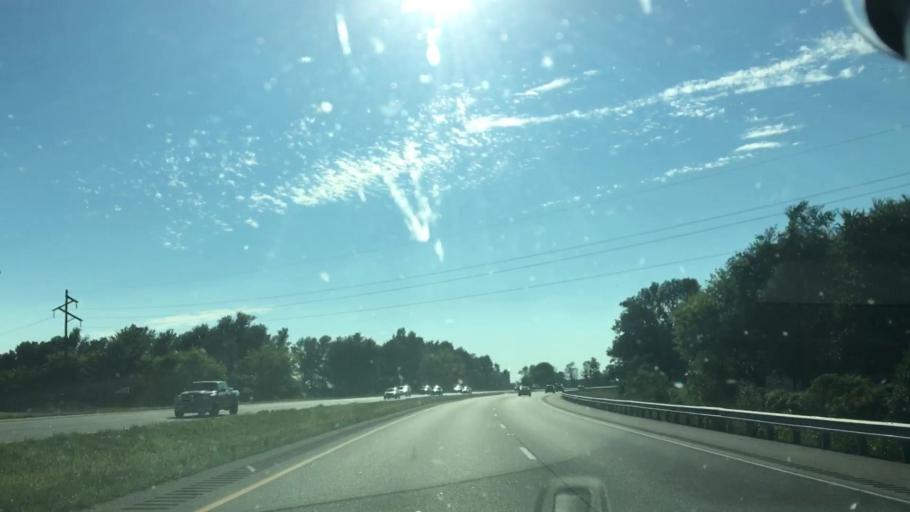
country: US
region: Kentucky
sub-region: Daviess County
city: Owensboro
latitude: 37.7259
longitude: -87.1001
